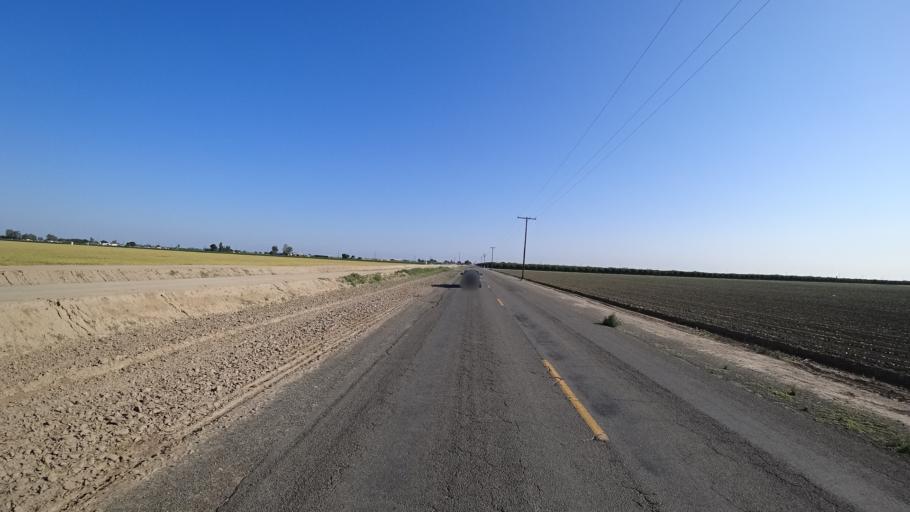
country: US
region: California
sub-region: Kings County
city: Home Garden
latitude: 36.3072
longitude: -119.5652
